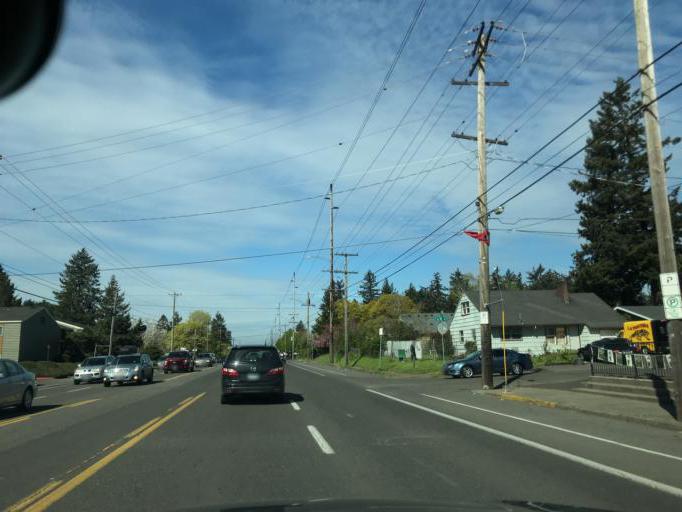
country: US
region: Oregon
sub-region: Multnomah County
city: Lents
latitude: 45.5042
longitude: -122.5424
